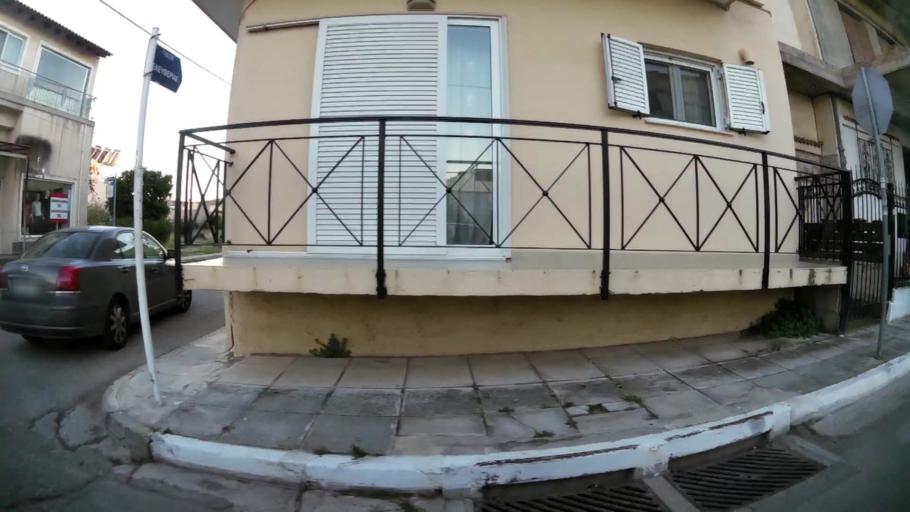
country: GR
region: Attica
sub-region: Nomarchia Dytikis Attikis
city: Ano Liosia
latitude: 38.0833
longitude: 23.7010
